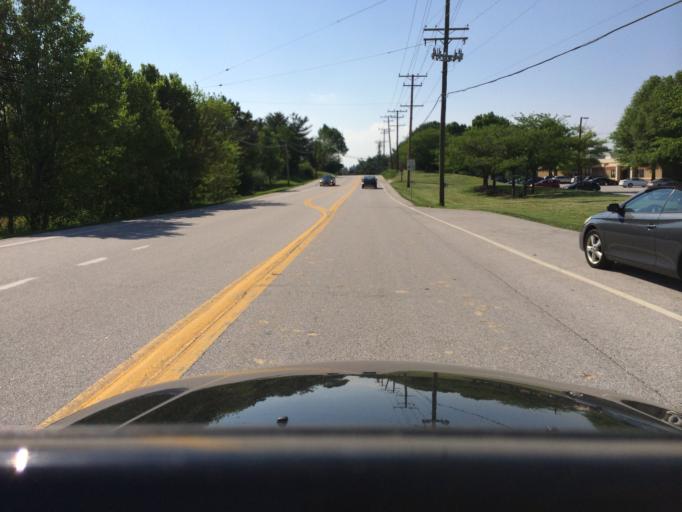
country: US
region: Maryland
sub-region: Howard County
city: Highland
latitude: 39.1897
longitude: -76.9258
